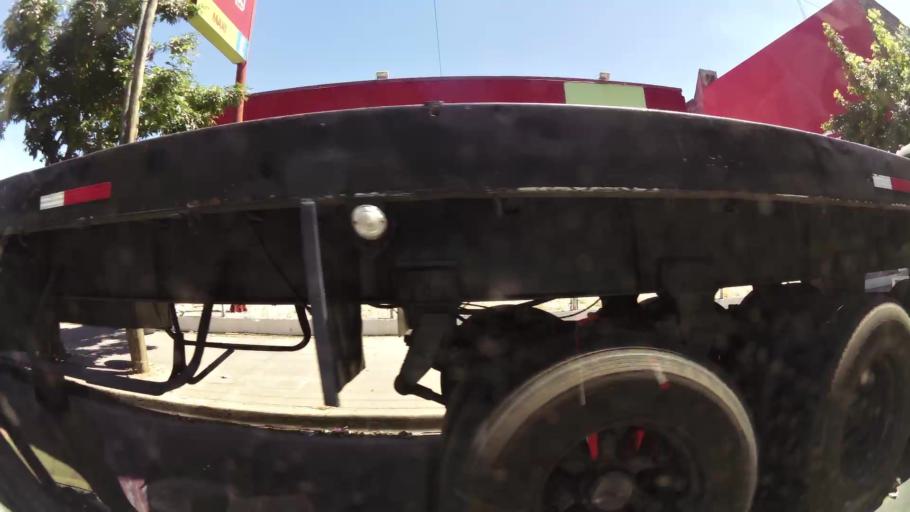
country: AR
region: Buenos Aires
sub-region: Partido de General San Martin
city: General San Martin
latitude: -34.5189
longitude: -58.5605
